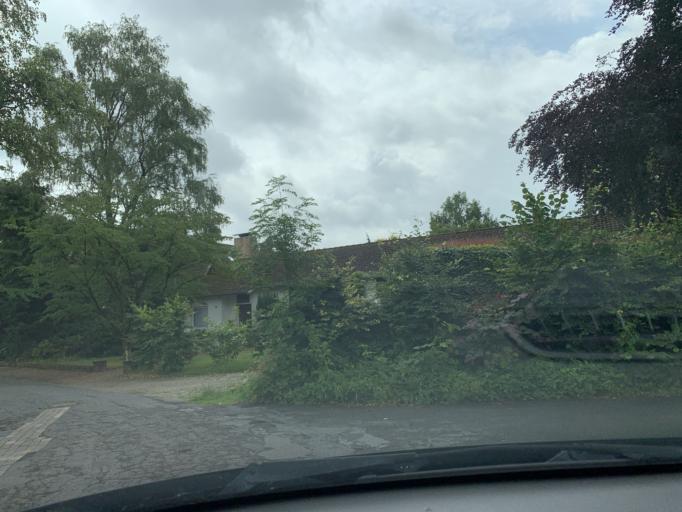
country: DE
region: Lower Saxony
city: Westerstede
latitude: 53.2517
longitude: 7.9216
